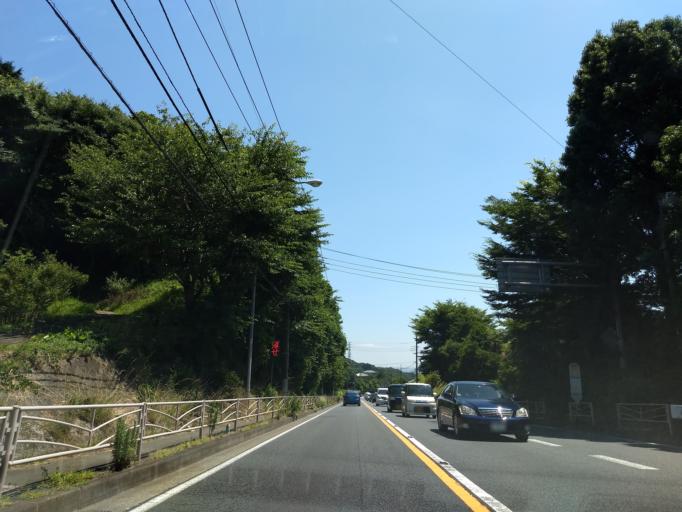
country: JP
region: Kanagawa
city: Hadano
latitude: 35.3880
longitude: 139.2624
